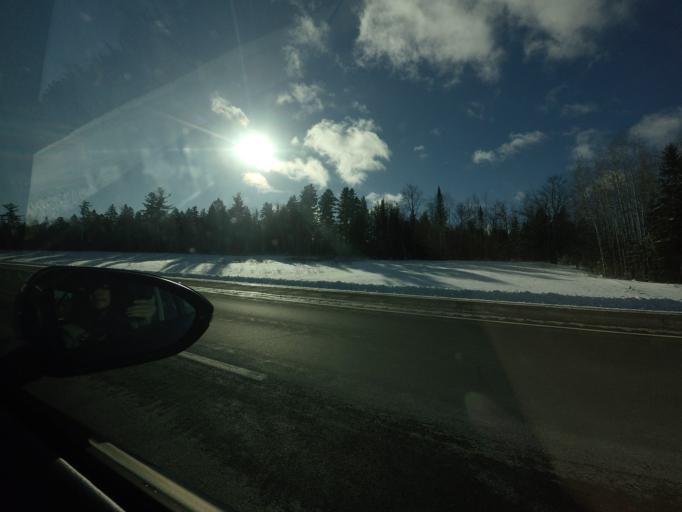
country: CA
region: New Brunswick
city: Fredericton
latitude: 45.8763
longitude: -66.6305
